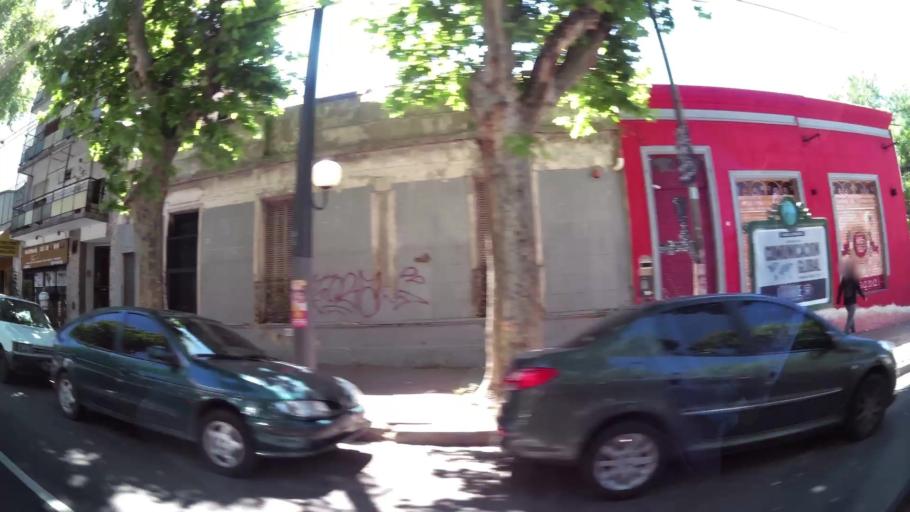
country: AR
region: Buenos Aires F.D.
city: Buenos Aires
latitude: -34.6325
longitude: -58.4160
